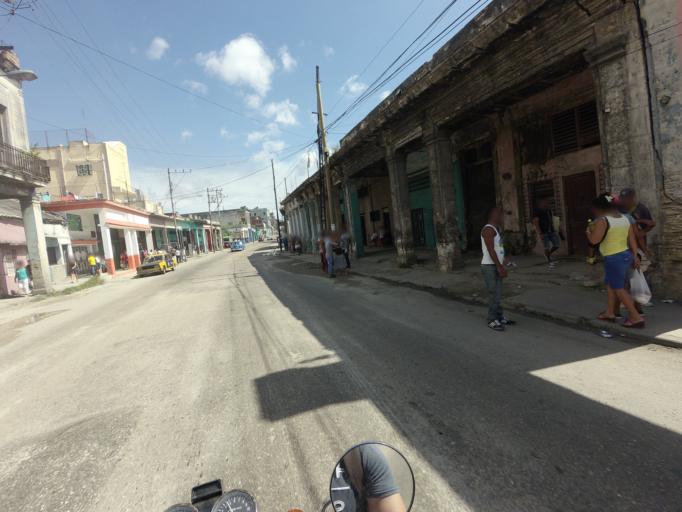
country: CU
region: La Habana
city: Diez de Octubre
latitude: 23.0953
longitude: -82.3638
